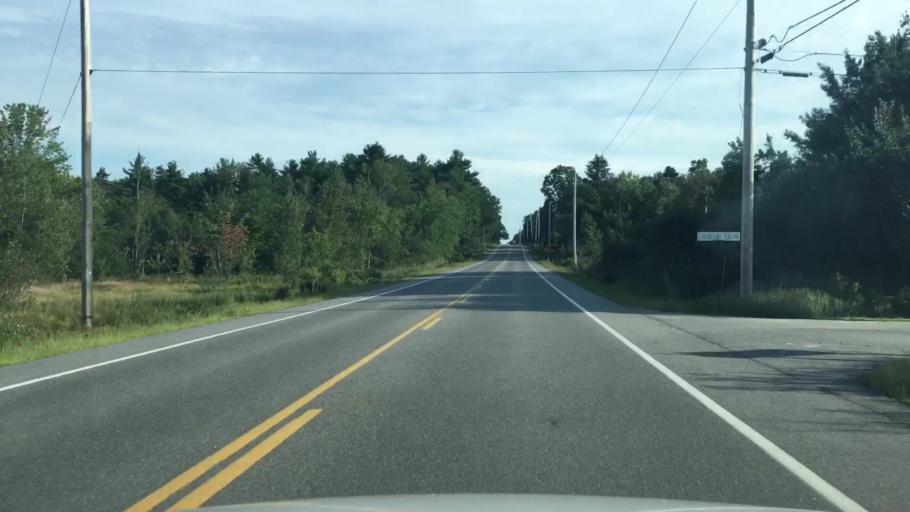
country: US
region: Maine
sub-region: Cumberland County
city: North Windham
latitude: 43.8167
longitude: -70.4413
